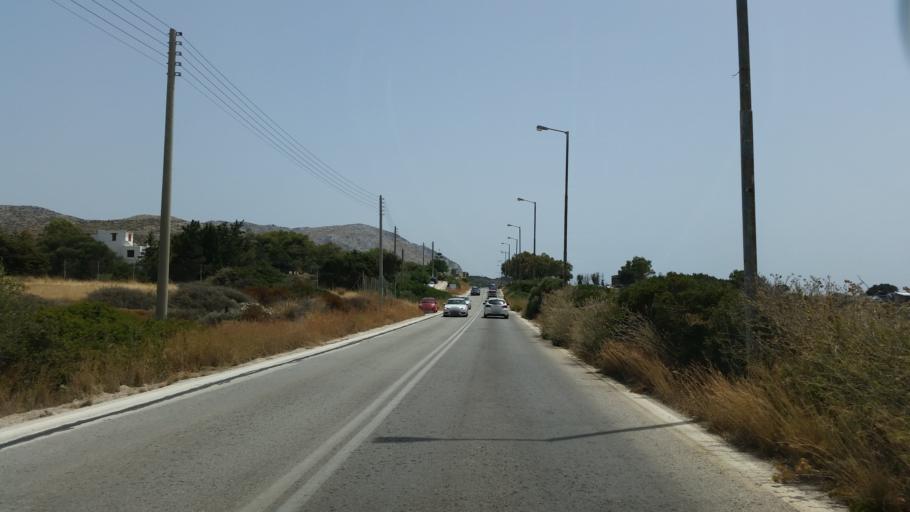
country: GR
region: Attica
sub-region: Nomarchia Anatolikis Attikis
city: Palaia Fokaia
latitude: 37.6964
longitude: 23.9384
